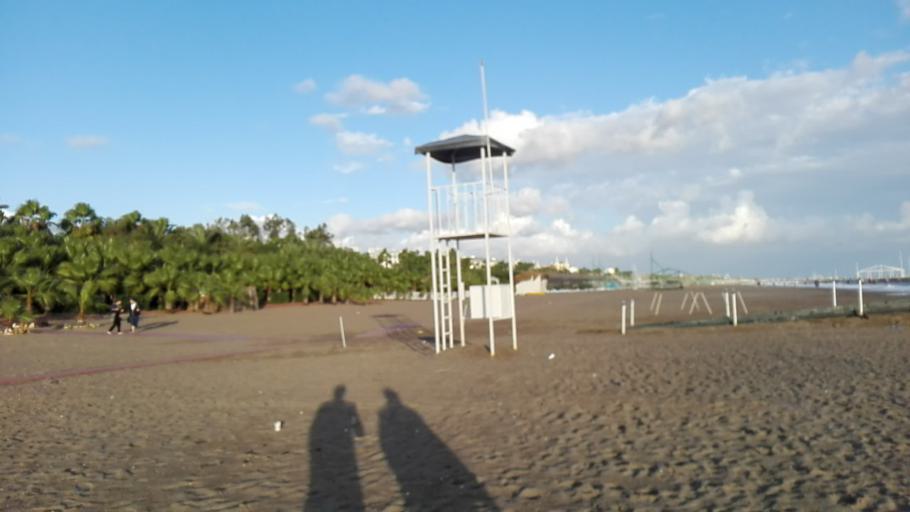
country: TR
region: Antalya
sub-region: Serik
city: Kumkoey
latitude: 36.8527
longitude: 30.8758
